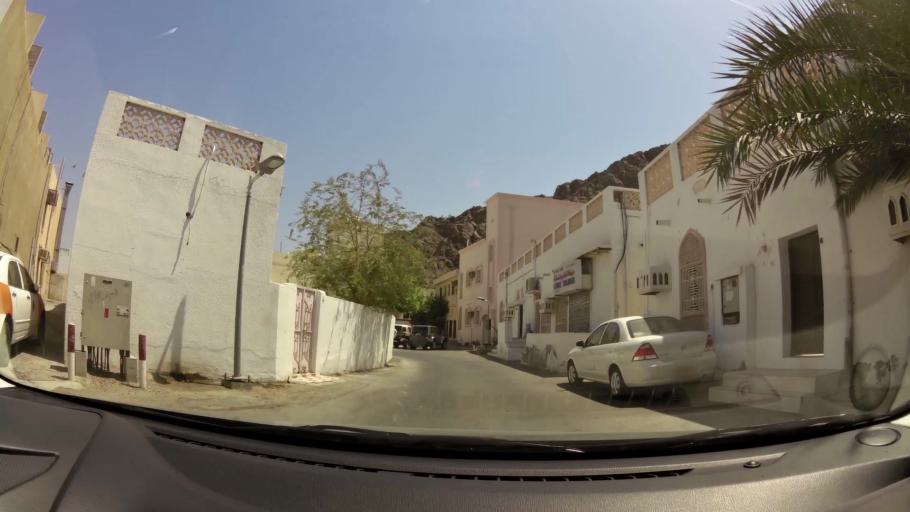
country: OM
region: Muhafazat Masqat
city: Muscat
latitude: 23.5942
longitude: 58.5974
